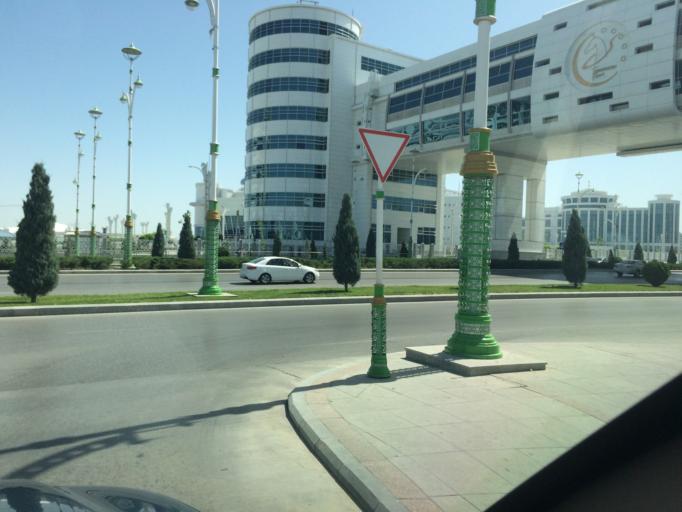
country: TM
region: Ahal
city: Ashgabat
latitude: 37.8960
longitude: 58.3718
